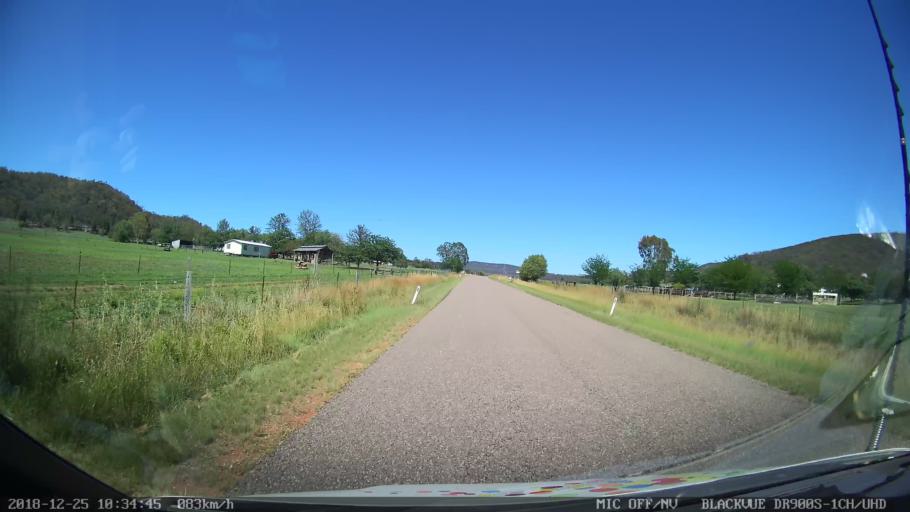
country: AU
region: New South Wales
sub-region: Upper Hunter Shire
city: Merriwa
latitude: -32.3938
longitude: 150.4039
